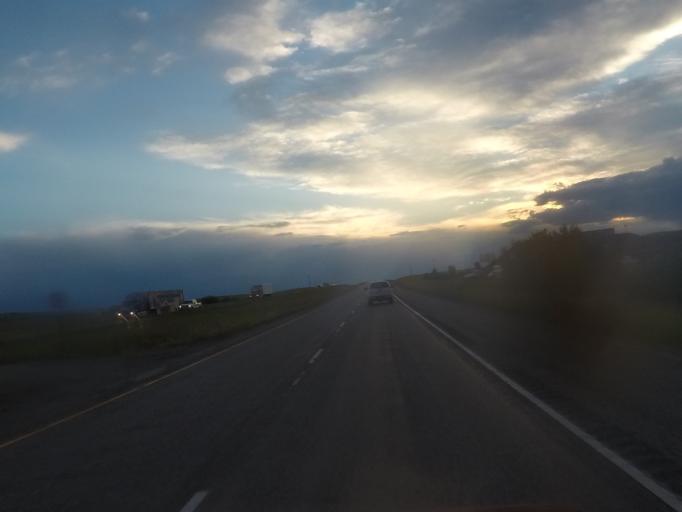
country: US
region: Montana
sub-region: Gallatin County
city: Bozeman
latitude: 45.6619
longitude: -110.9565
